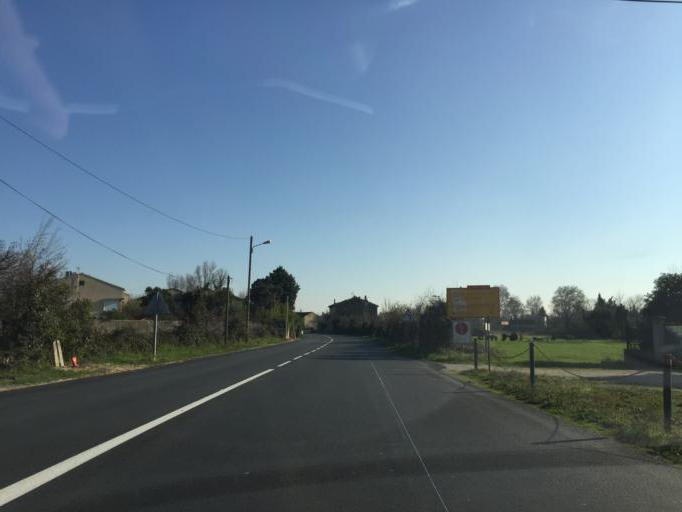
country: FR
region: Provence-Alpes-Cote d'Azur
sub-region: Departement du Vaucluse
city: Jonquieres
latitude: 44.1164
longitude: 4.8885
